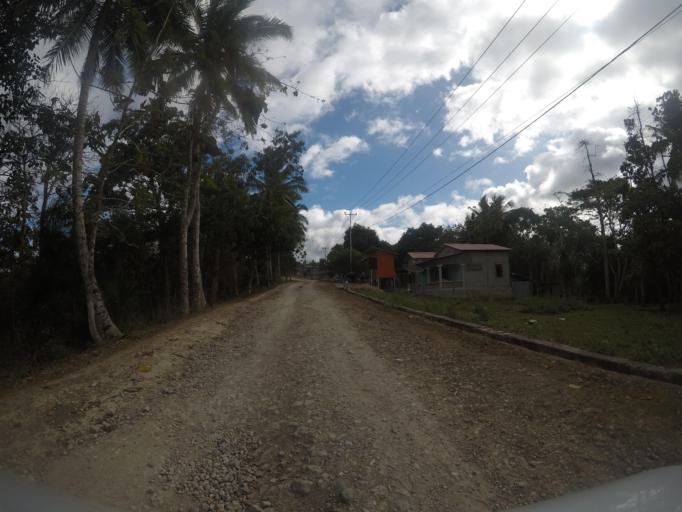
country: TL
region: Lautem
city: Lospalos
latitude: -8.5672
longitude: 126.8855
